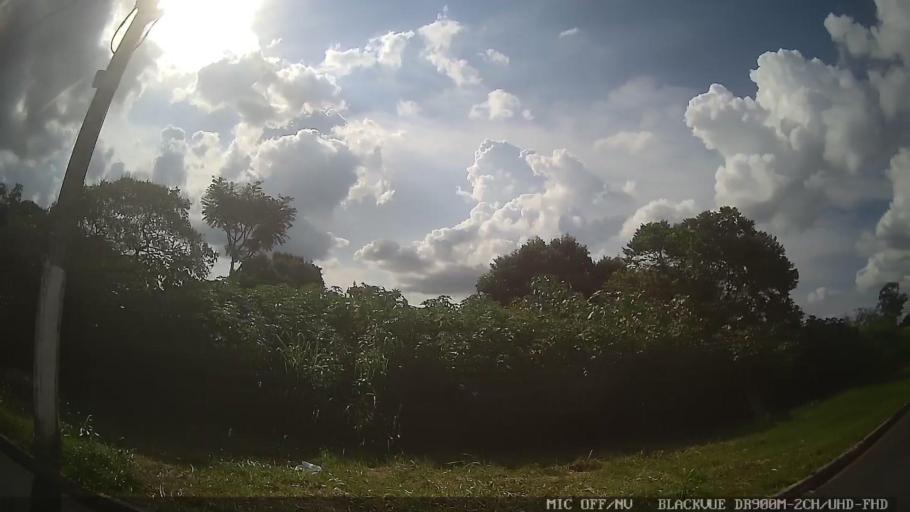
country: BR
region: Sao Paulo
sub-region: Atibaia
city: Atibaia
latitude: -23.1308
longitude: -46.5773
